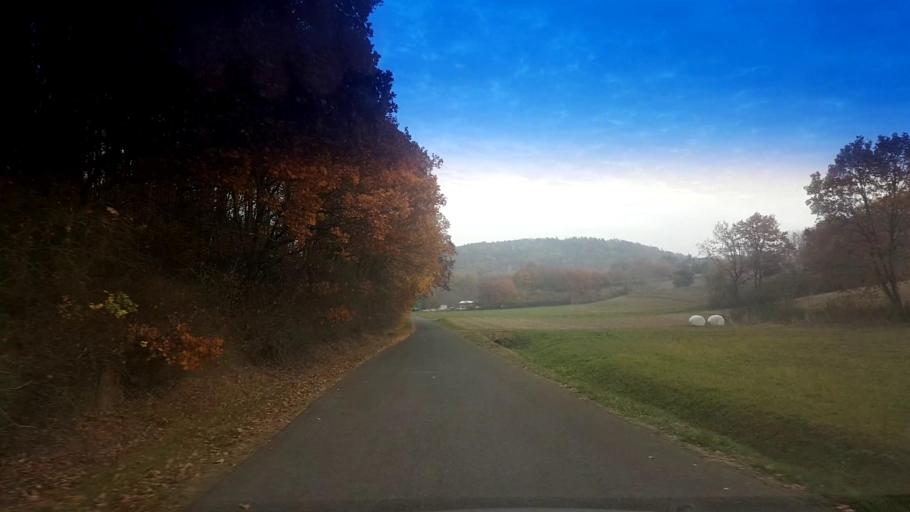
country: DE
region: Bavaria
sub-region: Upper Franconia
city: Viereth-Trunstadt
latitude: 49.9210
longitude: 10.7589
